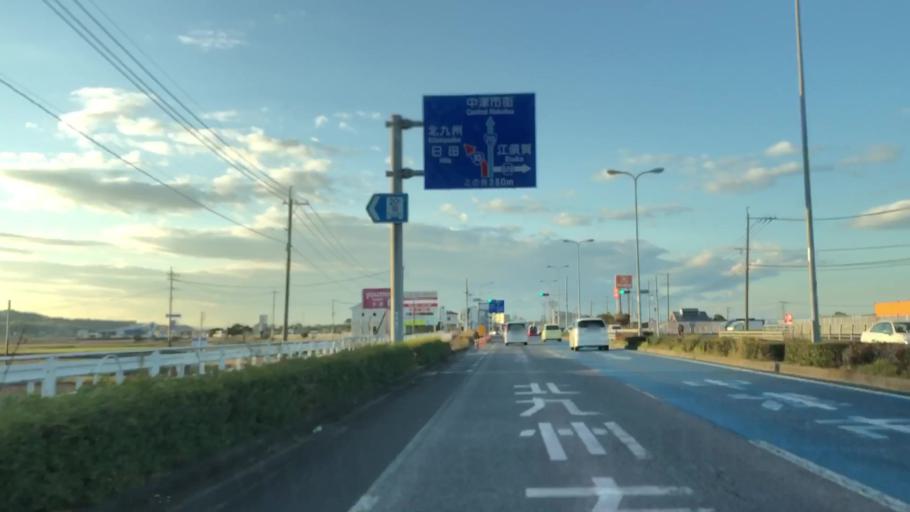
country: JP
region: Fukuoka
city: Nakatsu
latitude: 33.5497
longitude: 131.2763
